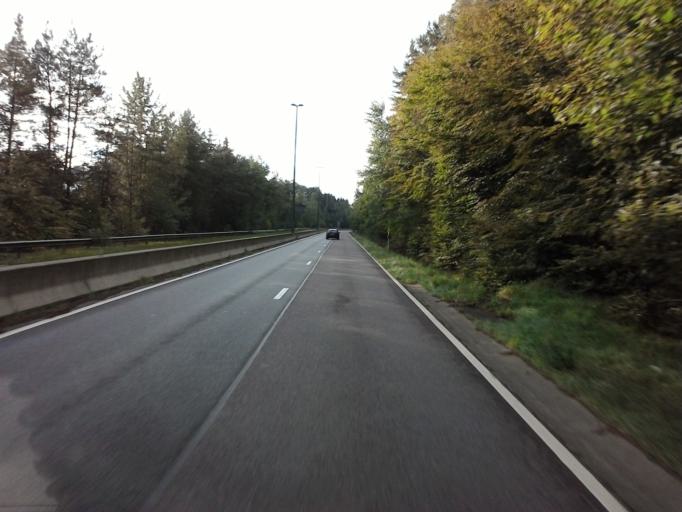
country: BE
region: Wallonia
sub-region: Province du Luxembourg
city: Attert
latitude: 49.7194
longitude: 5.8001
